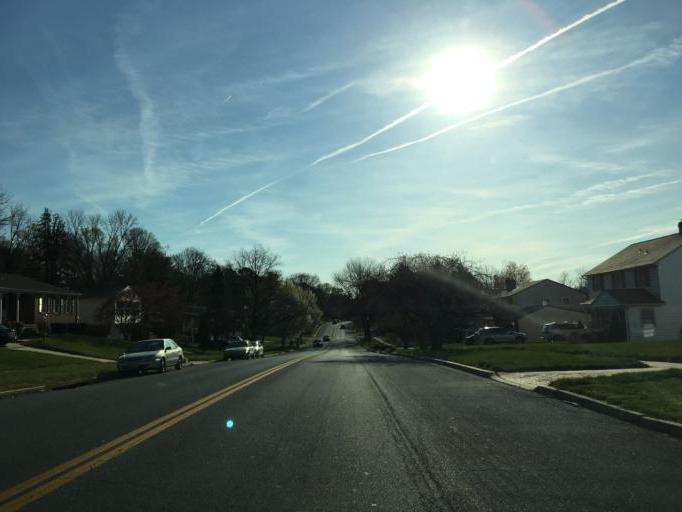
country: US
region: Maryland
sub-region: Baltimore County
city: Timonium
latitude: 39.4464
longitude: -76.6129
